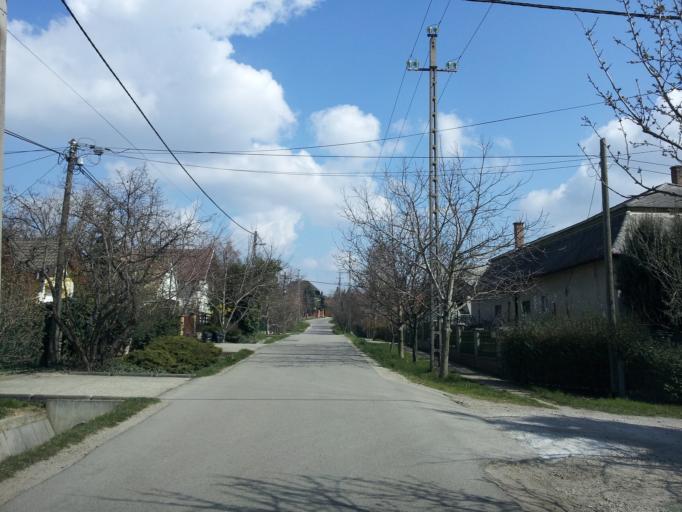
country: HU
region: Pest
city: Erd
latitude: 47.3935
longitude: 18.9209
